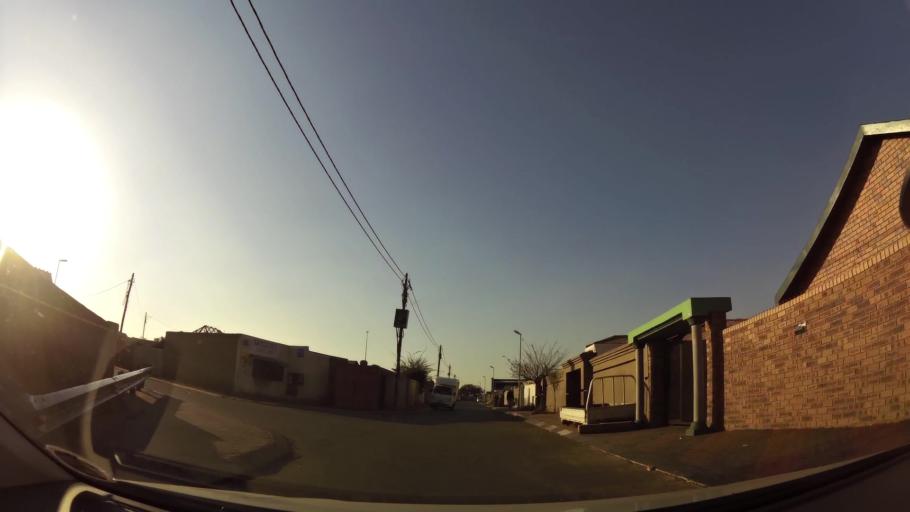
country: ZA
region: Gauteng
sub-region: City of Johannesburg Metropolitan Municipality
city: Soweto
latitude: -26.2595
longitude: 27.8803
